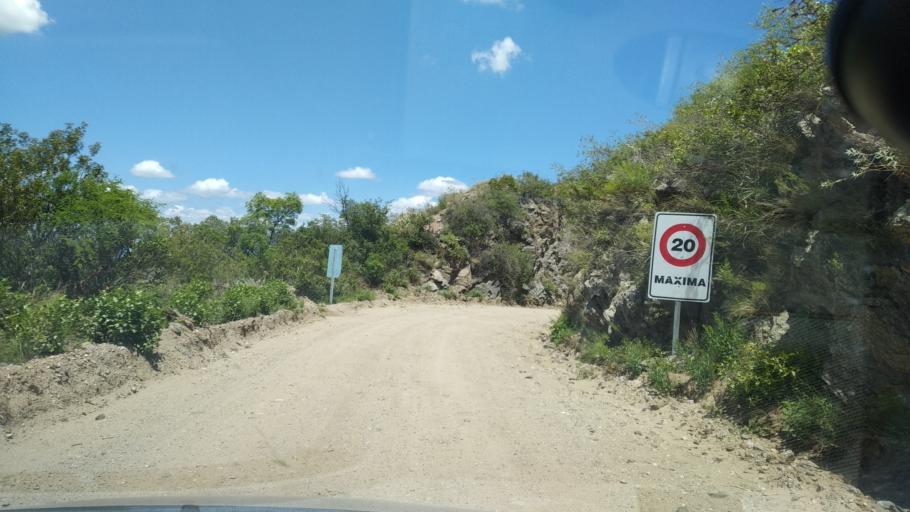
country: AR
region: Cordoba
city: Salsacate
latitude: -31.3772
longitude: -65.4023
